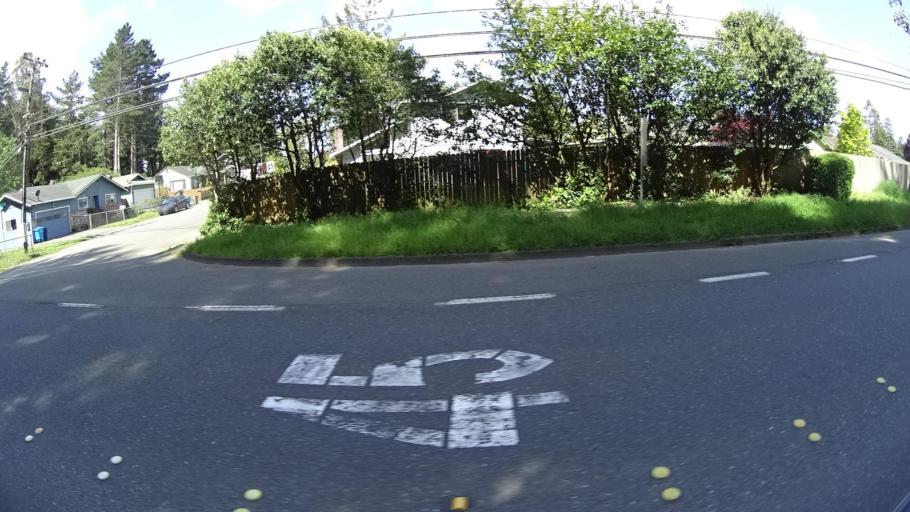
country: US
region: California
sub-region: Humboldt County
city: Cutten
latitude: 40.7567
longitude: -124.1469
